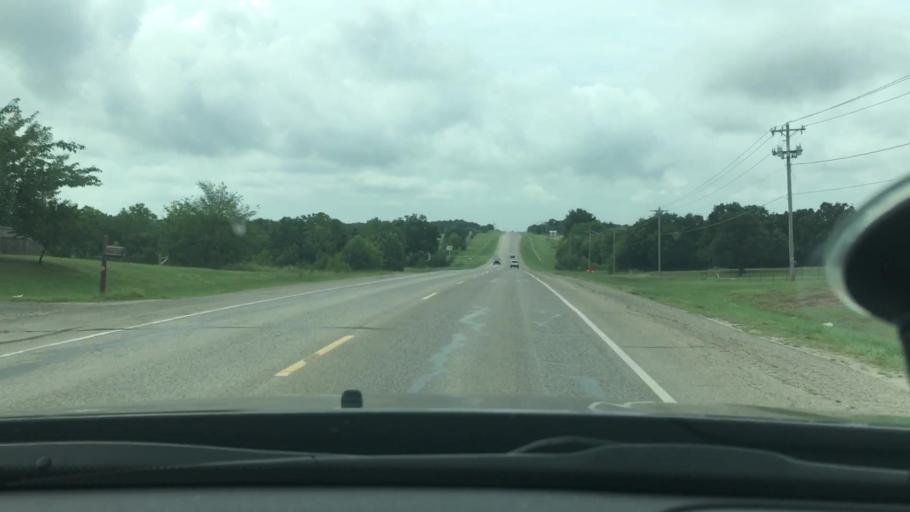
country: US
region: Oklahoma
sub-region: Carter County
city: Healdton
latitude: 34.2091
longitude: -97.4748
